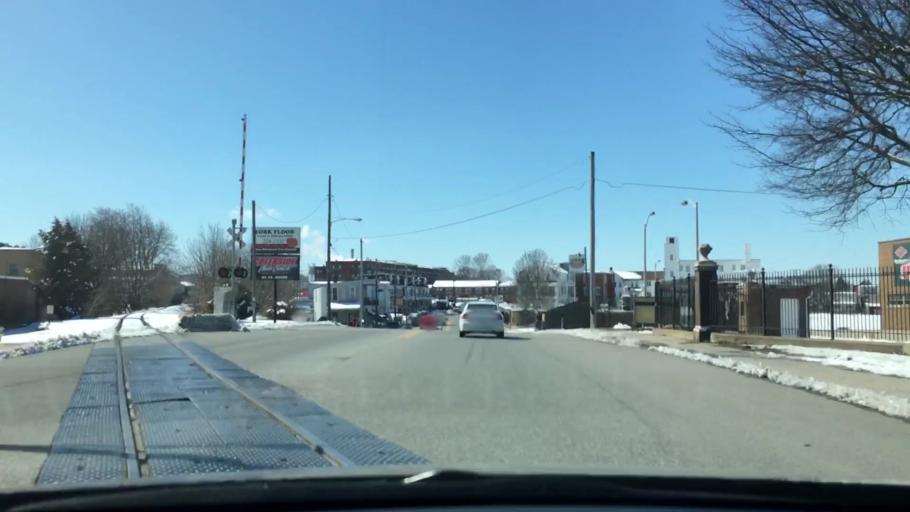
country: US
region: Pennsylvania
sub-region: York County
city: West York
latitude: 39.9547
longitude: -76.7531
